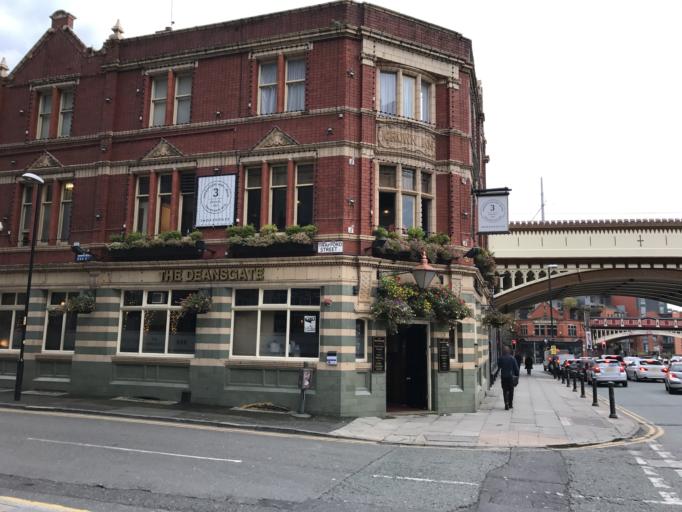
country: GB
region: England
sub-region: Manchester
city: Hulme
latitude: 53.4752
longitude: -2.2512
